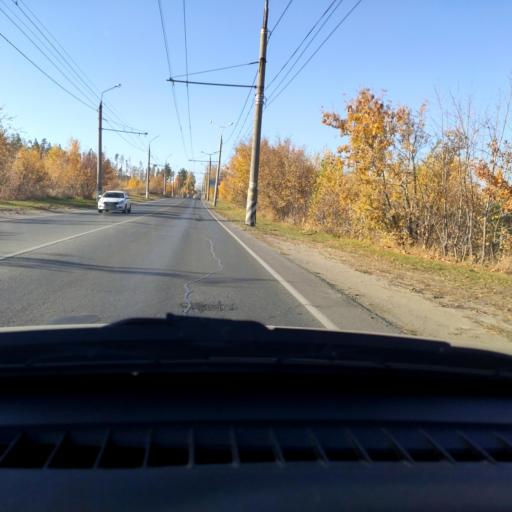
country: RU
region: Samara
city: Tol'yatti
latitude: 53.4822
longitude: 49.3754
